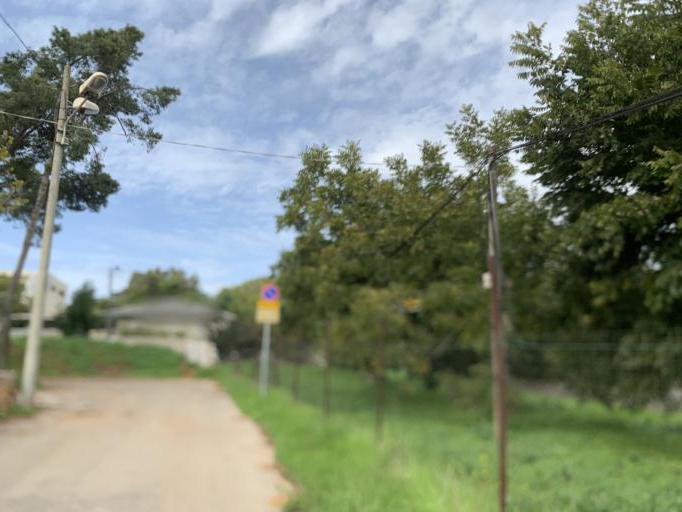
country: IL
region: Central District
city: Hod HaSharon
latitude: 32.1541
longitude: 34.9010
